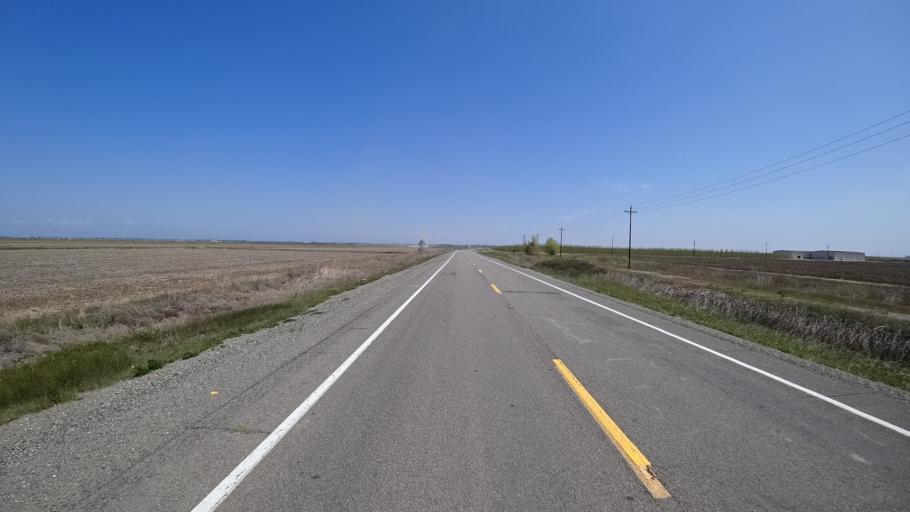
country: US
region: California
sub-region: Glenn County
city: Willows
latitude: 39.5217
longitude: -122.0635
